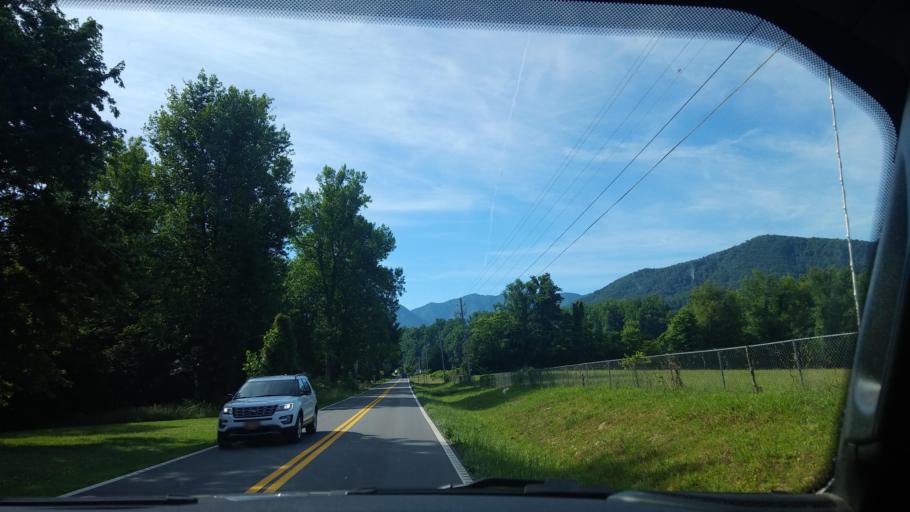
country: US
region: Tennessee
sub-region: Cocke County
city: Newport
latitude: 35.7914
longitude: -83.2334
